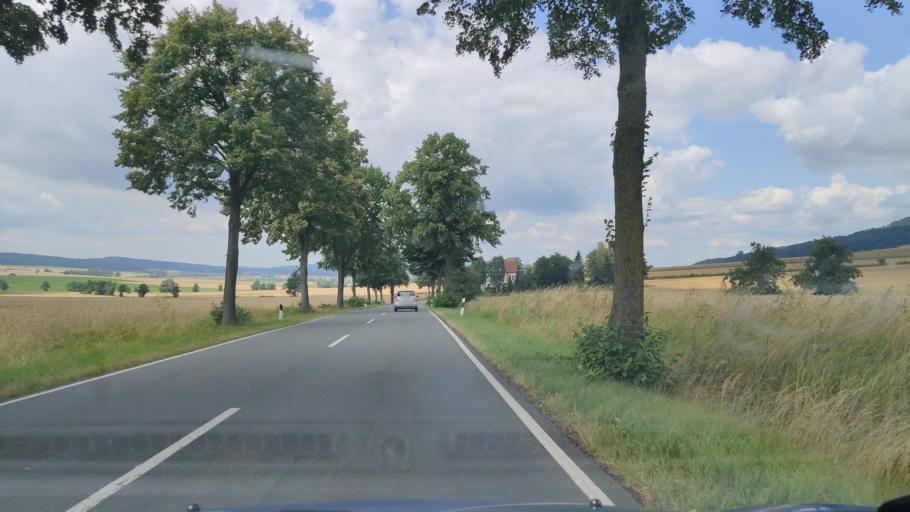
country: DE
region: Lower Saxony
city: Heyen
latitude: 52.0649
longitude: 9.5226
